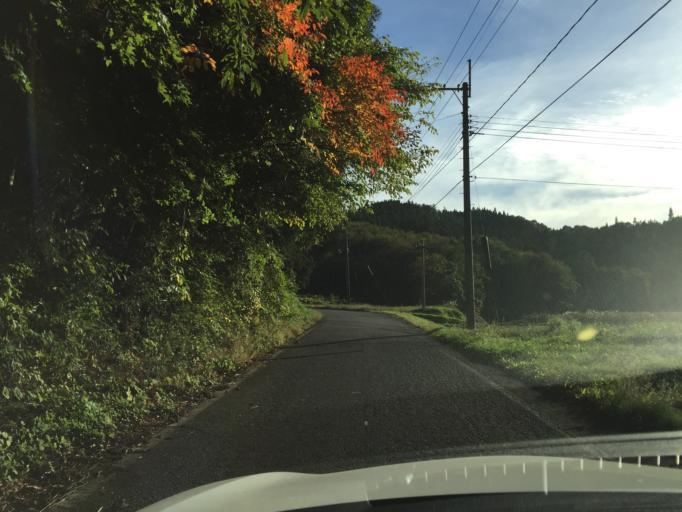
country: JP
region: Fukushima
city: Ishikawa
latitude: 37.2452
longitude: 140.6078
